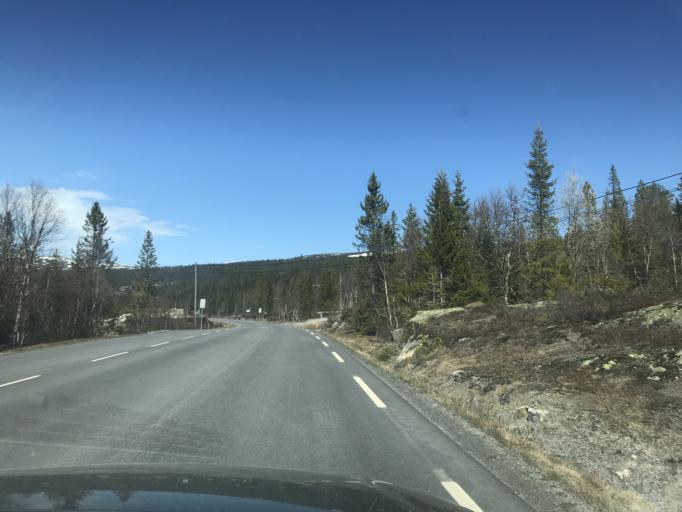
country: NO
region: Telemark
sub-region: Tinn
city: Rjukan
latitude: 59.7783
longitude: 8.7716
